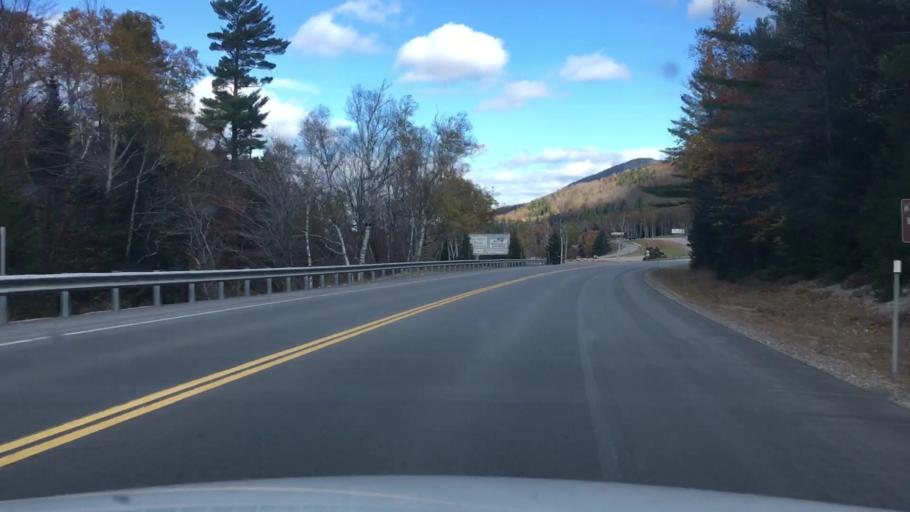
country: US
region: New Hampshire
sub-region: Coos County
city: Gorham
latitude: 44.2859
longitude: -71.2293
